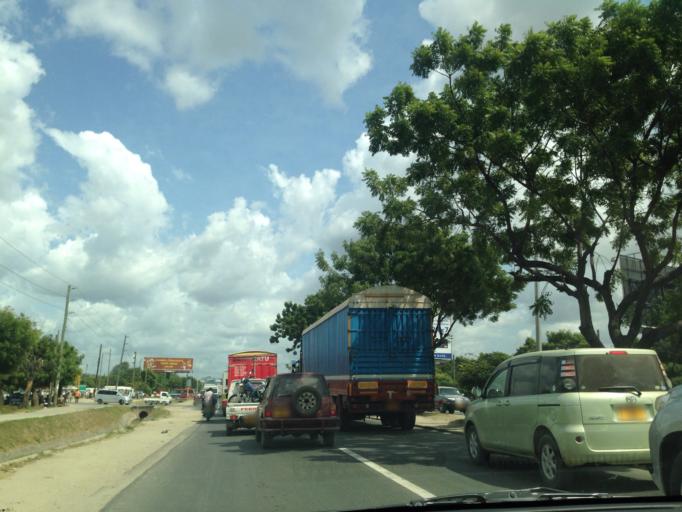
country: TZ
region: Dar es Salaam
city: Dar es Salaam
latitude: -6.8312
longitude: 39.2702
